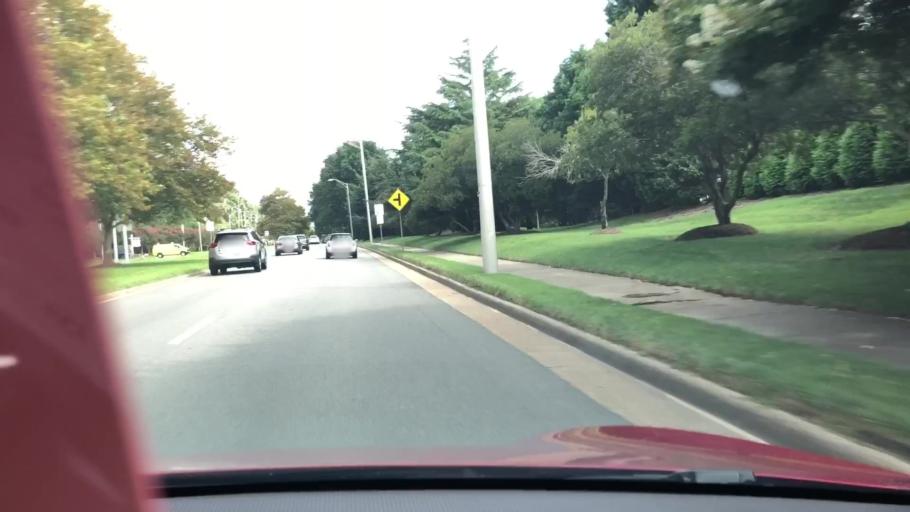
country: US
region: Virginia
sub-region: City of Virginia Beach
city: Virginia Beach
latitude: 36.8946
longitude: -76.0595
